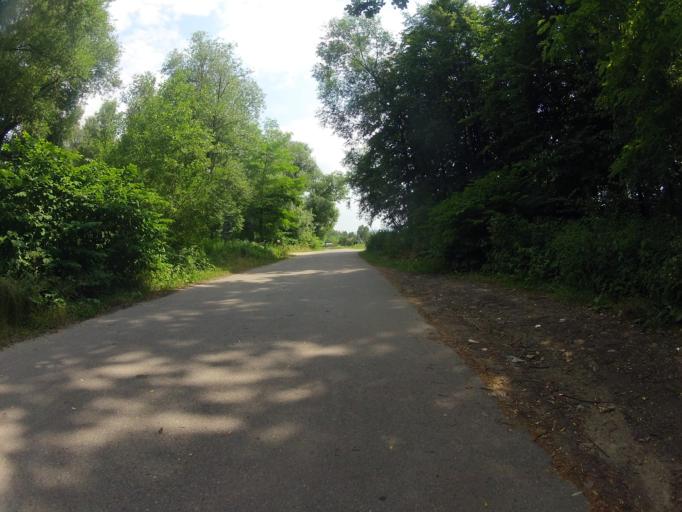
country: PL
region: Lesser Poland Voivodeship
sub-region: Powiat nowosadecki
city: Stary Sacz
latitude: 49.5614
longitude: 20.6596
